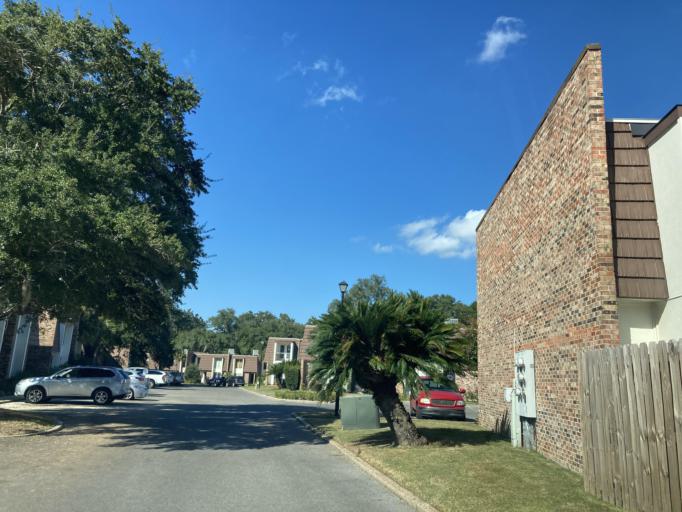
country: US
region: Mississippi
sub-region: Jackson County
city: Ocean Springs
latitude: 30.4043
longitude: -88.8260
